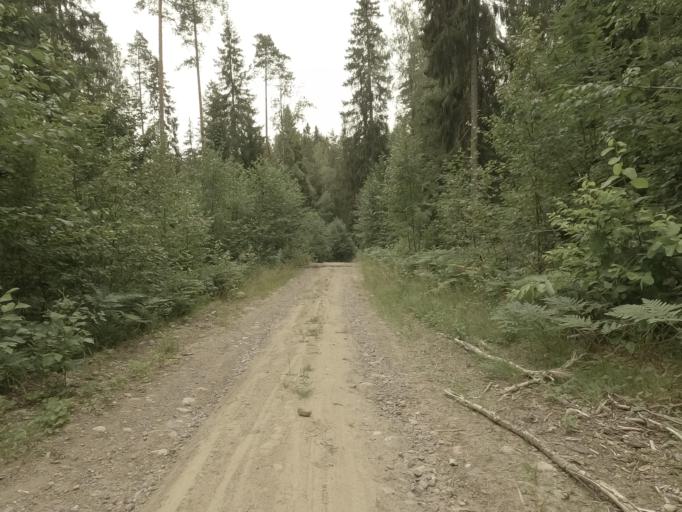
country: RU
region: Leningrad
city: Kamennogorsk
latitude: 61.0711
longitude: 29.1664
